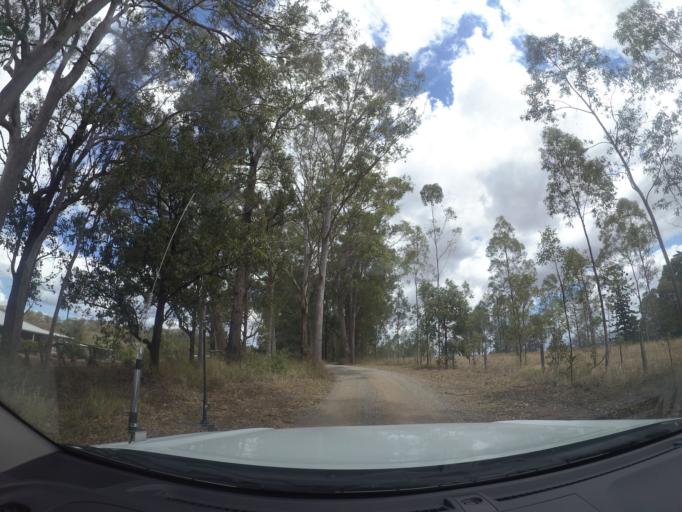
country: AU
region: Queensland
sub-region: Logan
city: Cedar Vale
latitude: -27.9094
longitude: 153.0315
